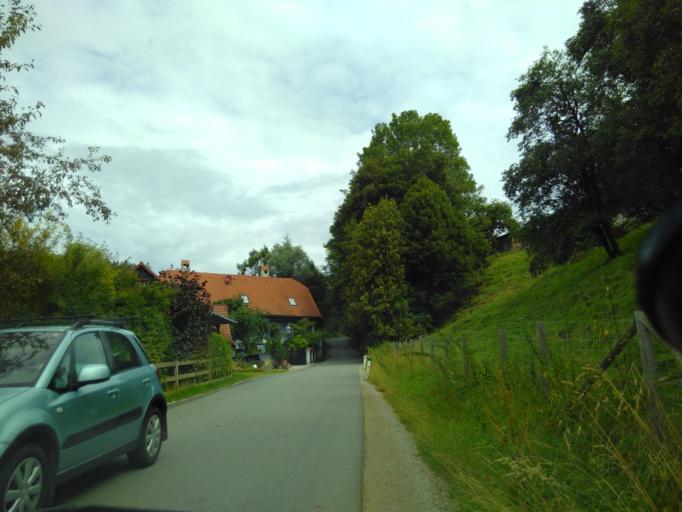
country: AT
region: Styria
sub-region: Politischer Bezirk Graz-Umgebung
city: Semriach
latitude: 47.2233
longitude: 15.3996
